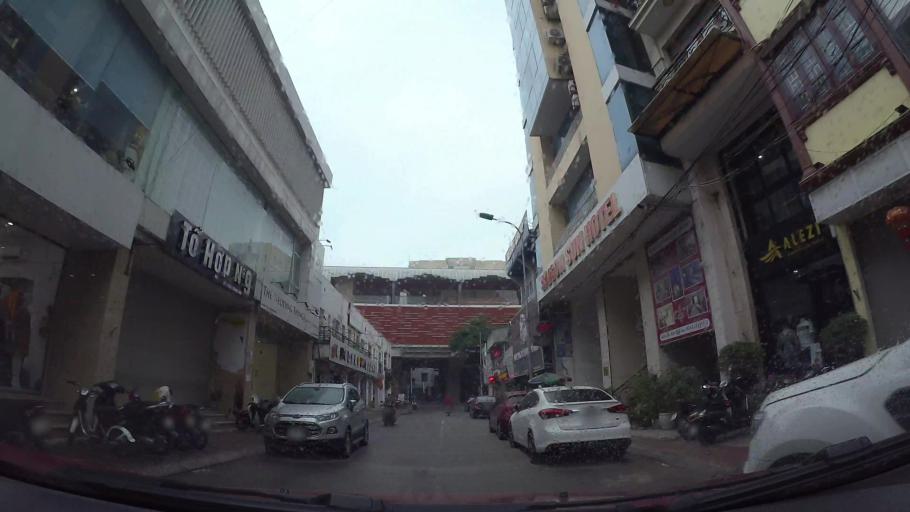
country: VN
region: Ha Noi
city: Dong Da
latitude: 21.0198
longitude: 105.8260
